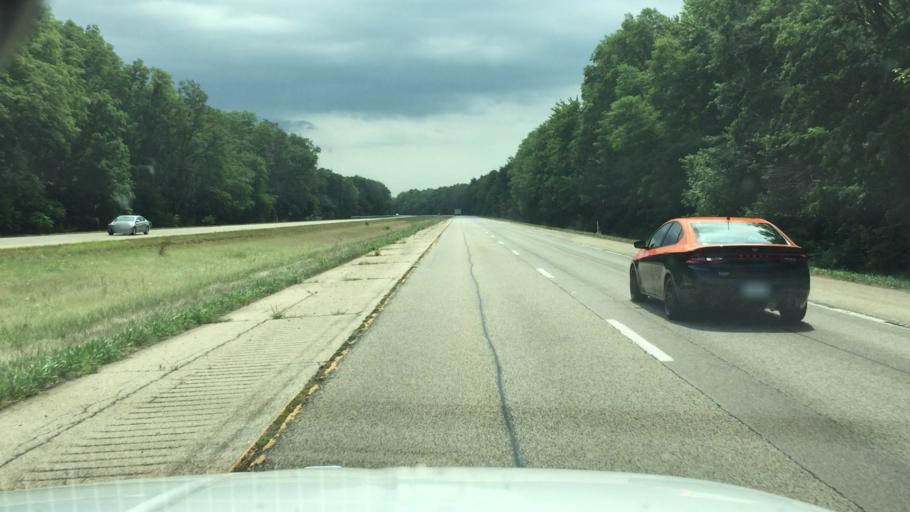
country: US
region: Illinois
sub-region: Peoria County
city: Hanna City
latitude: 40.8078
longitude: -89.8320
